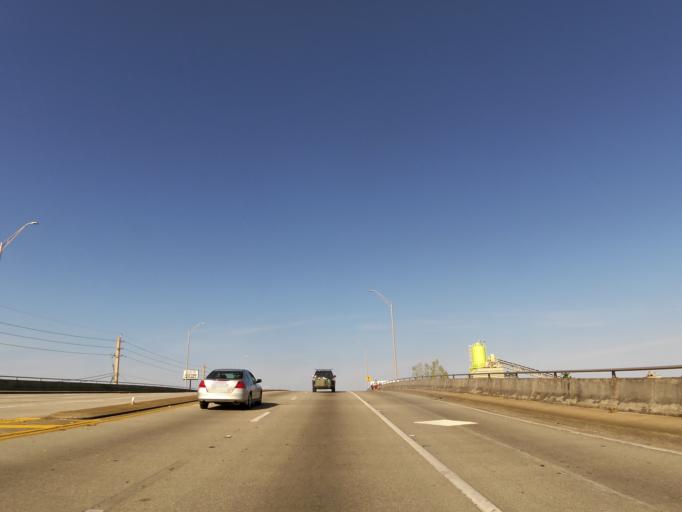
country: US
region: Florida
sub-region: Duval County
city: Jacksonville
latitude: 30.2643
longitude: -81.6210
